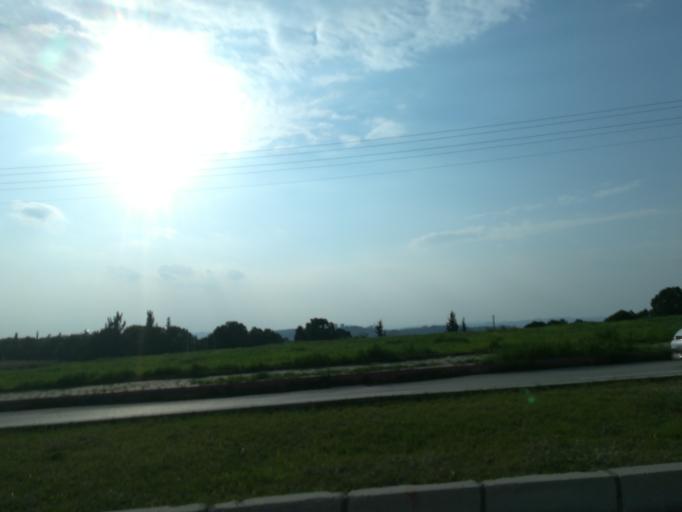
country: TR
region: Adana
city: Adana
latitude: 37.0772
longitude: 35.3884
